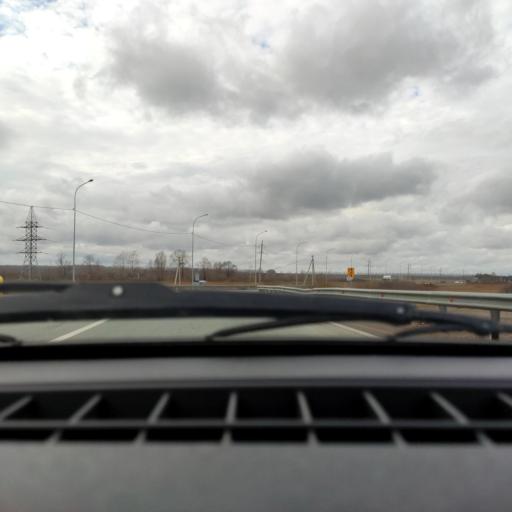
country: RU
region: Bashkortostan
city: Asanovo
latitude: 54.9102
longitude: 55.5998
